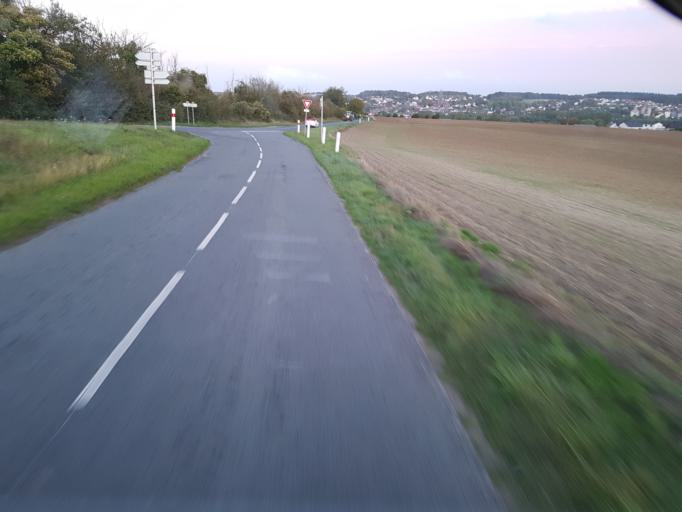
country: FR
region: Picardie
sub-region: Departement de la Somme
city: Ailly-sur-Noye
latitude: 49.7596
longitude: 2.3425
